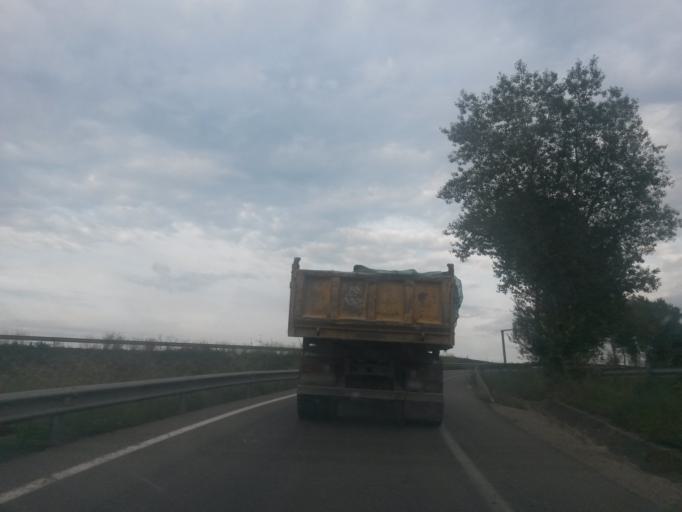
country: ES
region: Catalonia
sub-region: Provincia de Girona
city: Banyoles
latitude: 42.1396
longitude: 2.7645
